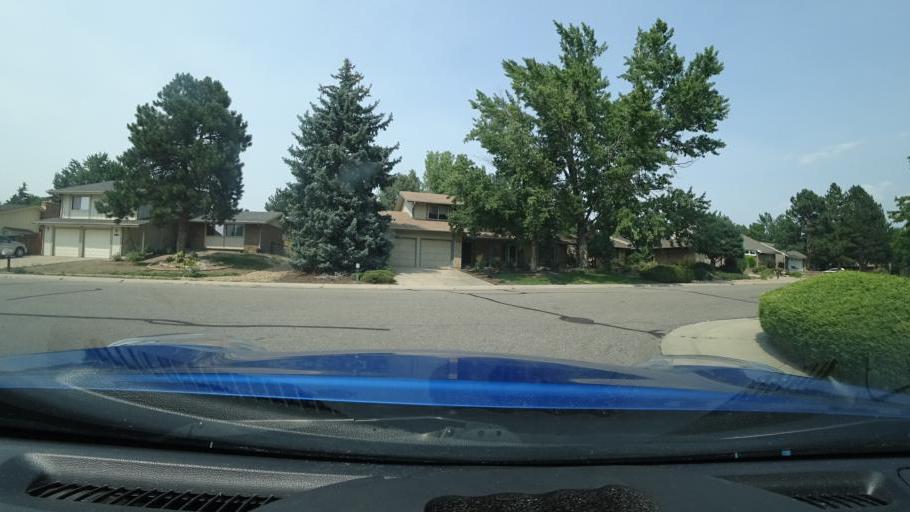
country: US
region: Colorado
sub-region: Adams County
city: Aurora
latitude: 39.6687
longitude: -104.8524
